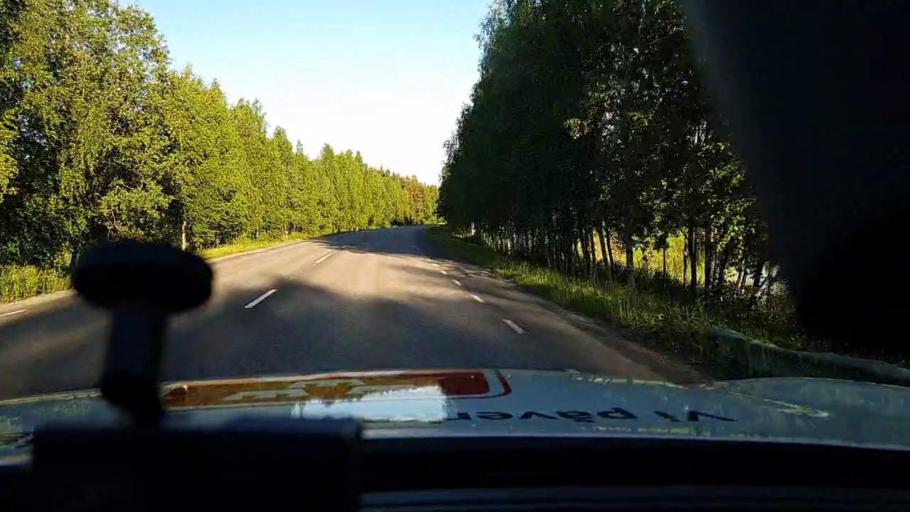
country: SE
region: Norrbotten
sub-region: Lulea Kommun
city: Lulea
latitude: 65.6119
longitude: 22.1619
